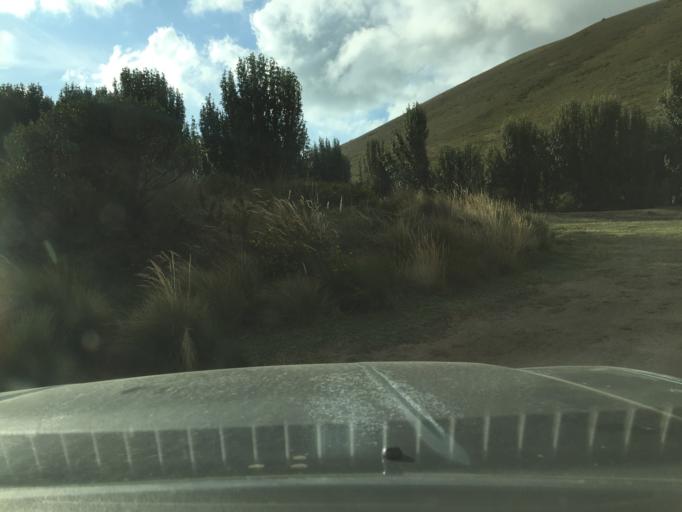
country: EC
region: Imbabura
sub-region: Canton Otavalo
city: Otavalo
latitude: 0.1134
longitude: -78.2765
